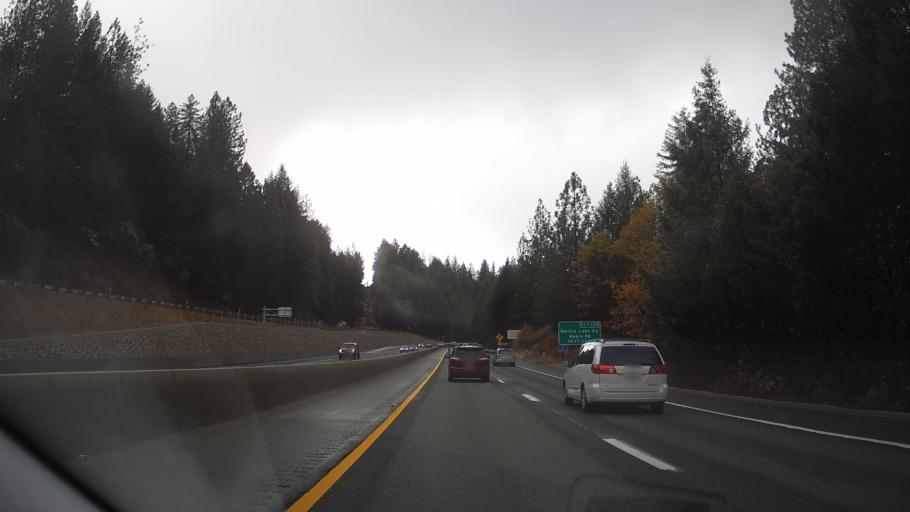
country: US
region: California
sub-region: Placer County
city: Colfax
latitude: 39.1490
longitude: -120.9004
